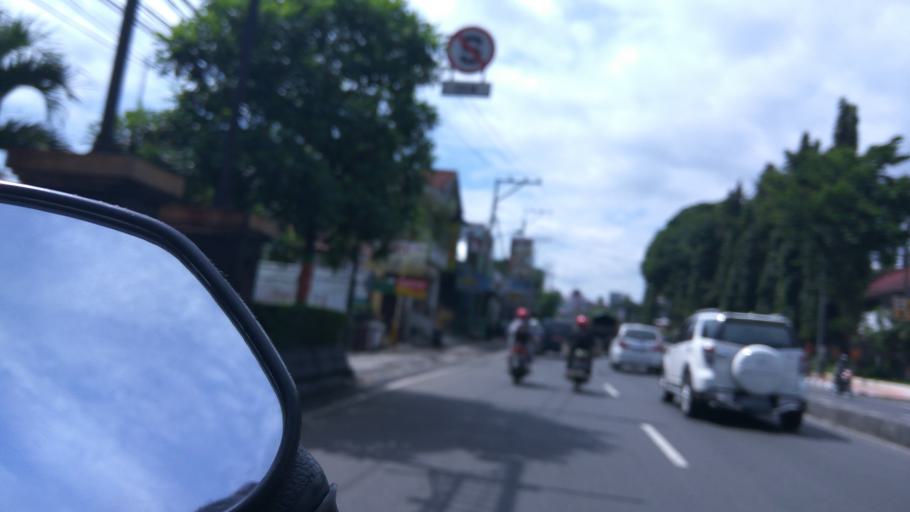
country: ID
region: Central Java
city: Ungaran
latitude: -7.1301
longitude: 110.4042
